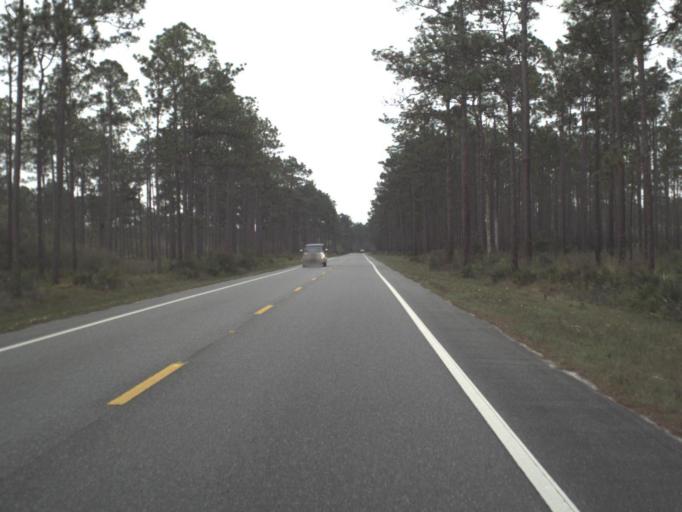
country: US
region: Florida
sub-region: Franklin County
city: Apalachicola
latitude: 29.9818
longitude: -84.9756
